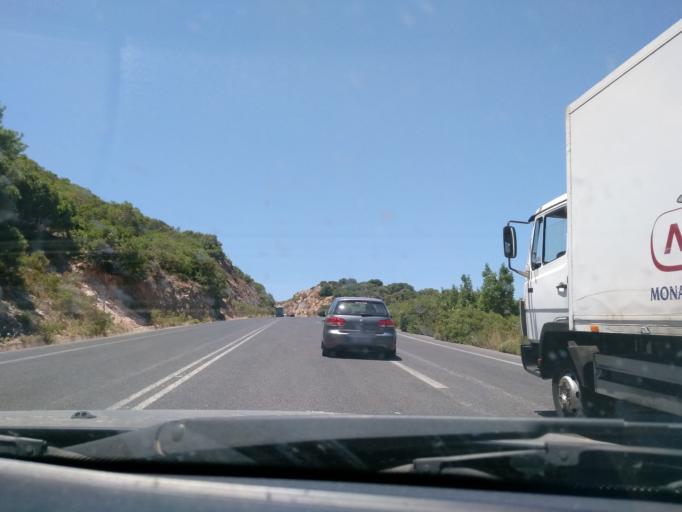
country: GR
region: Crete
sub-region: Nomos Rethymnis
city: Anogeia
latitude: 35.3872
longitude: 24.9158
